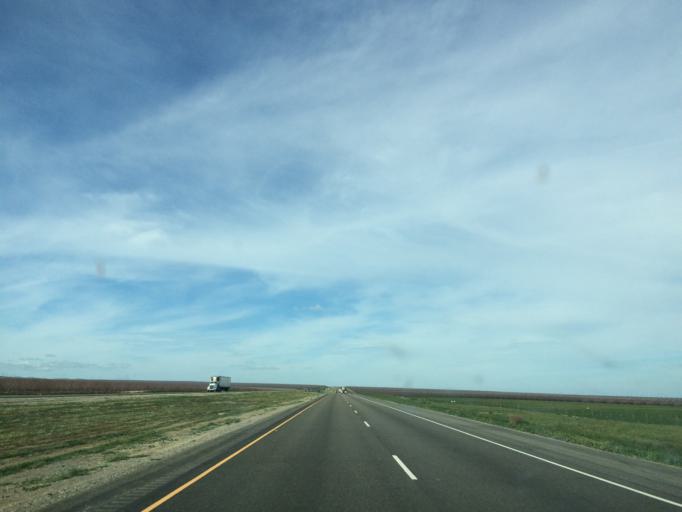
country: US
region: California
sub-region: Merced County
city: South Dos Palos
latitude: 36.7217
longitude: -120.6852
